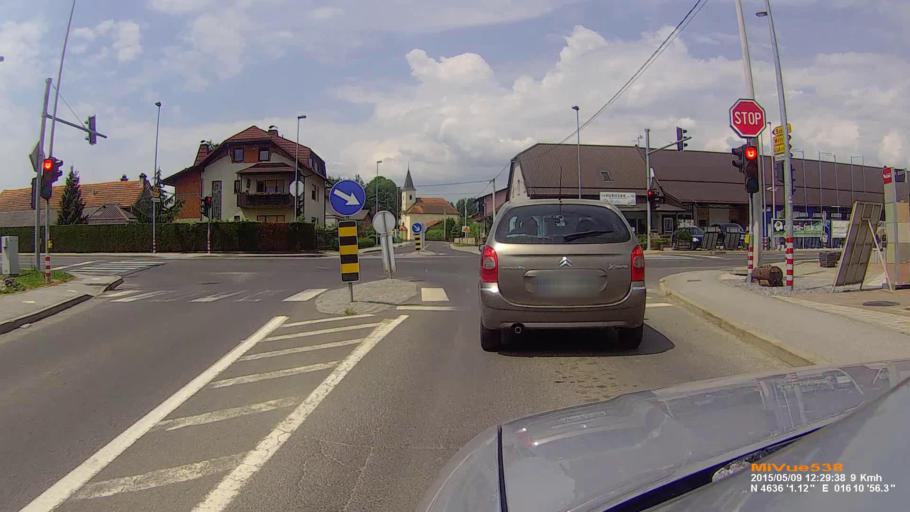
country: SI
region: Verzej
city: Verzej
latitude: 46.6003
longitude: 16.1827
